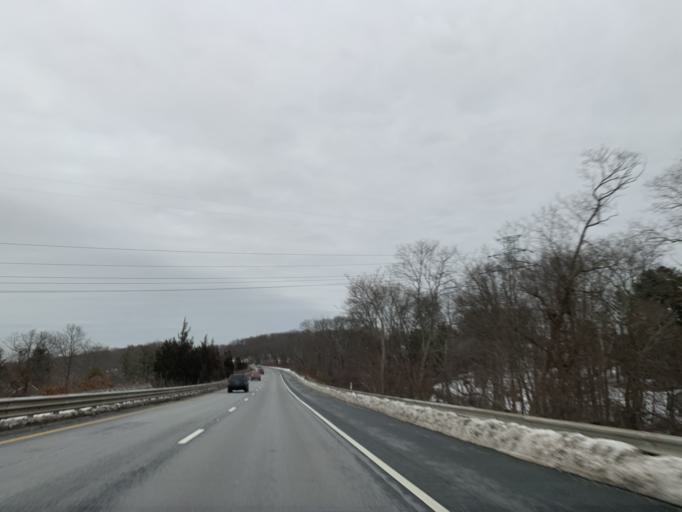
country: US
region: Massachusetts
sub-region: Bristol County
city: Somerset
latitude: 41.7387
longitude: -71.1269
